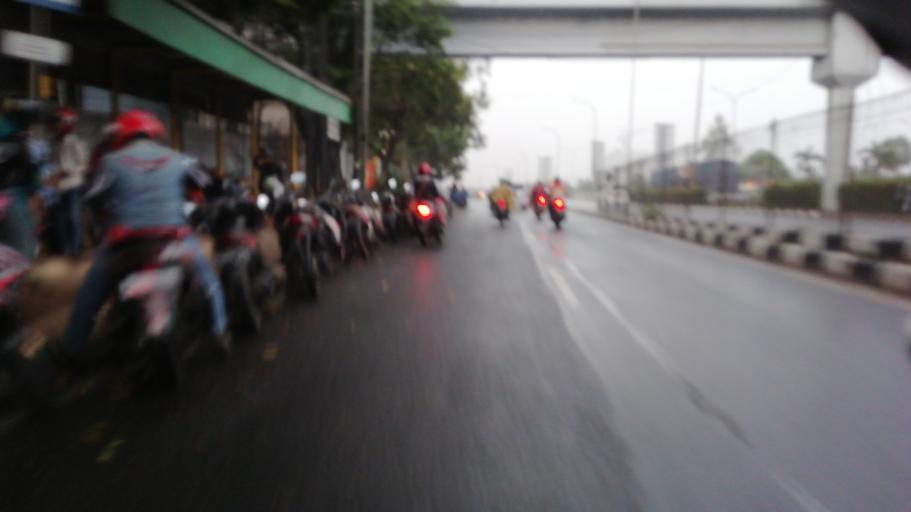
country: ID
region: Jakarta Raya
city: Jakarta
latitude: -6.3010
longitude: 106.8359
